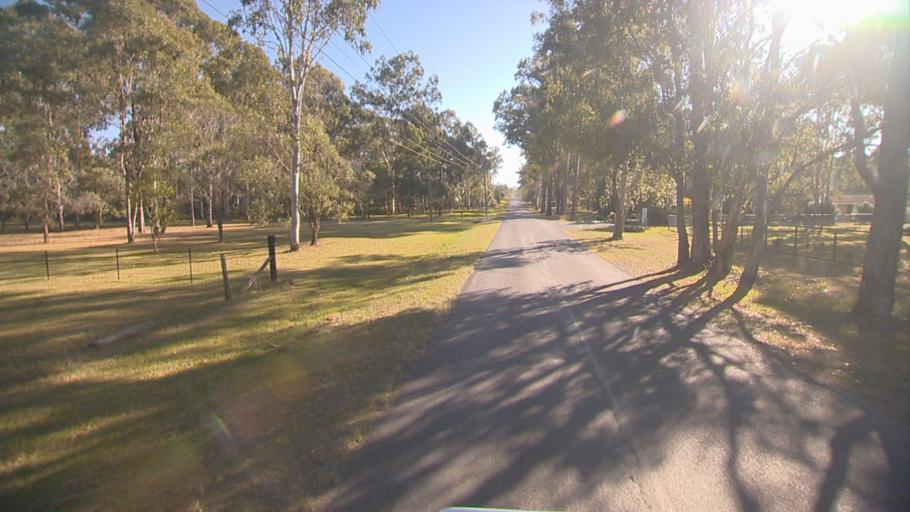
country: AU
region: Queensland
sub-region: Logan
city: Logan Reserve
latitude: -27.7416
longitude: 153.1081
